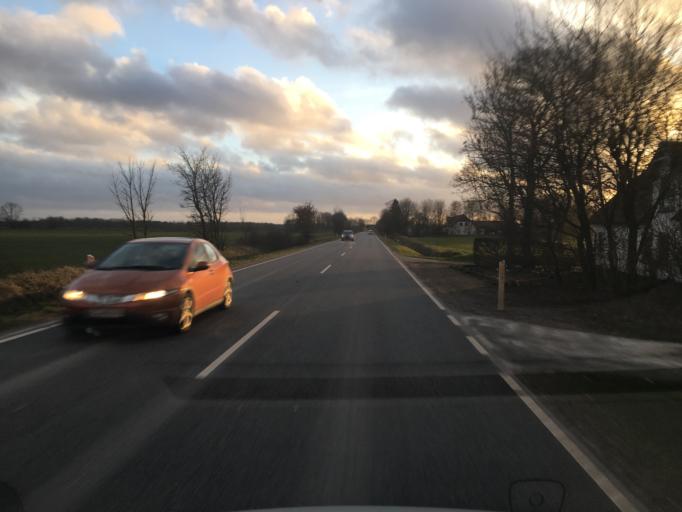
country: DK
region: South Denmark
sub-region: Aabenraa Kommune
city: Tinglev
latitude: 54.9590
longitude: 9.2899
